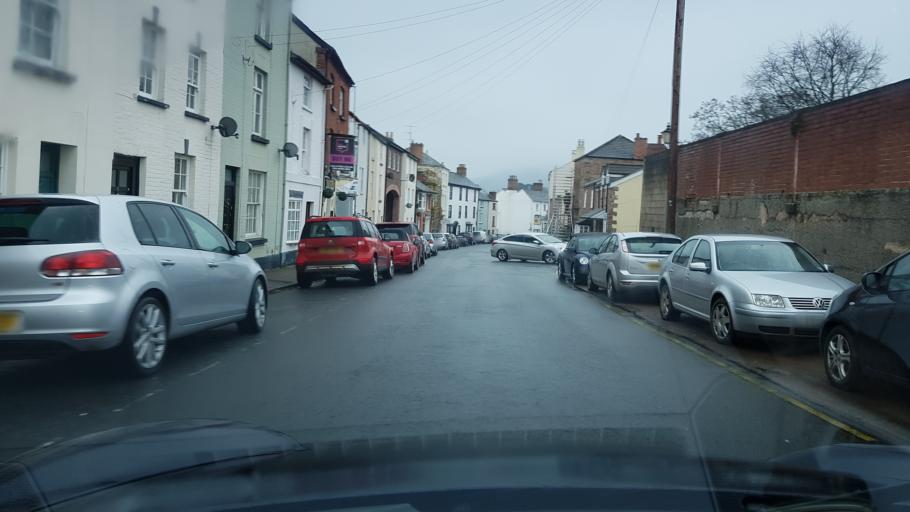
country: GB
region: England
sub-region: Herefordshire
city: Ross on Wye
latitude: 51.9156
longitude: -2.5855
